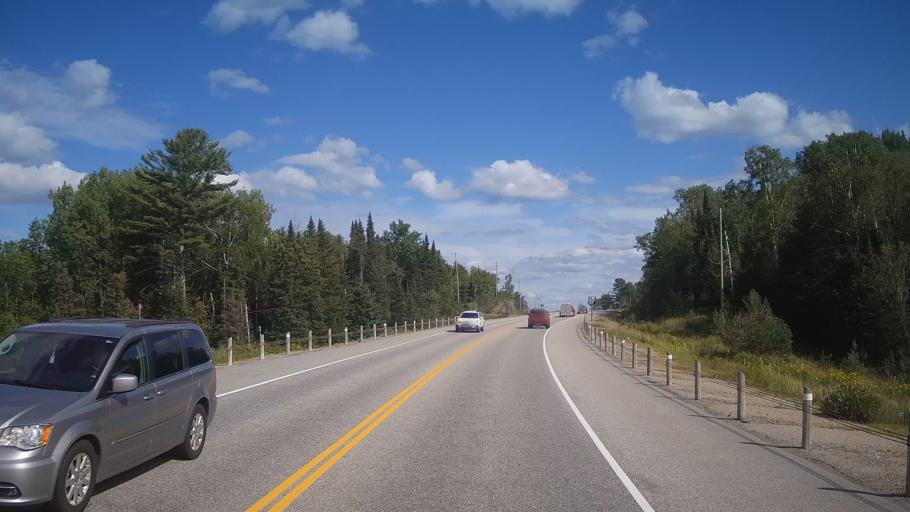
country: CA
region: Ontario
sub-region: Nipissing District
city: North Bay
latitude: 46.3024
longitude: -79.3815
